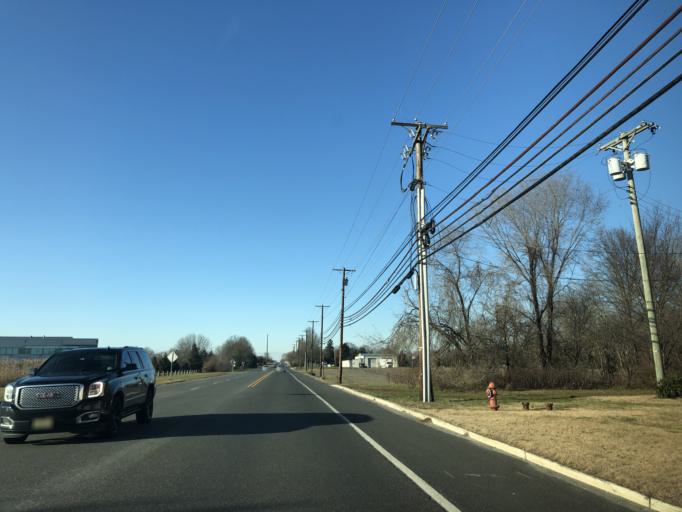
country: US
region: New Jersey
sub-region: Salem County
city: Carneys Point
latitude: 39.7035
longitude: -75.4412
